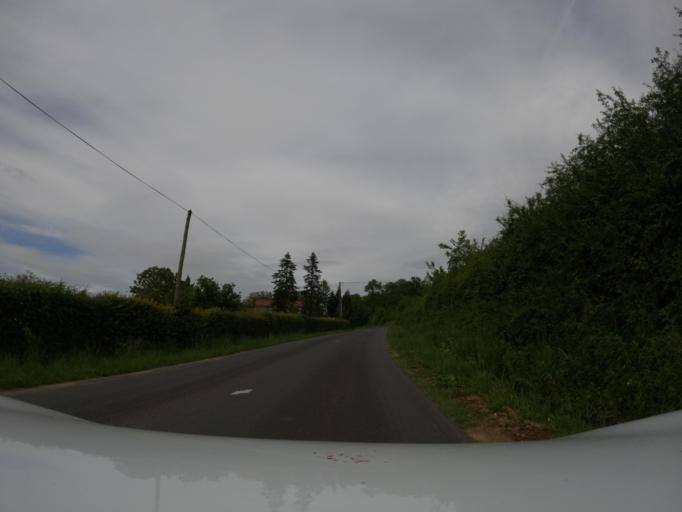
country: FR
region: Pays de la Loire
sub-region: Departement de la Vendee
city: Foussais-Payre
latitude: 46.5151
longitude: -0.6502
